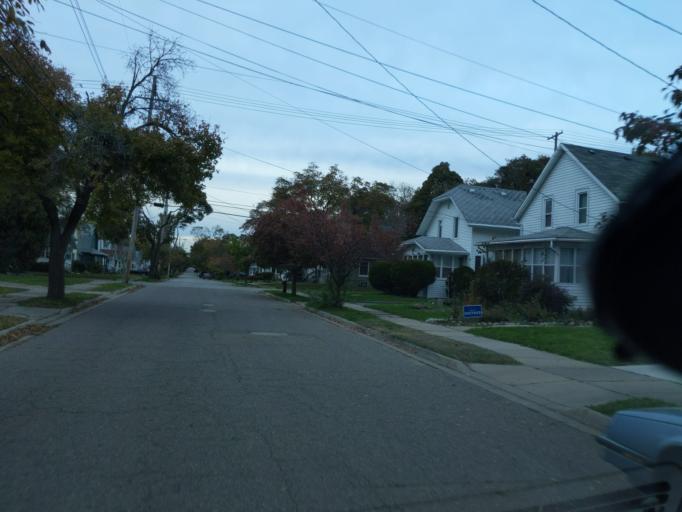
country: US
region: Michigan
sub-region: Ingham County
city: Lansing
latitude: 42.7356
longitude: -84.5200
